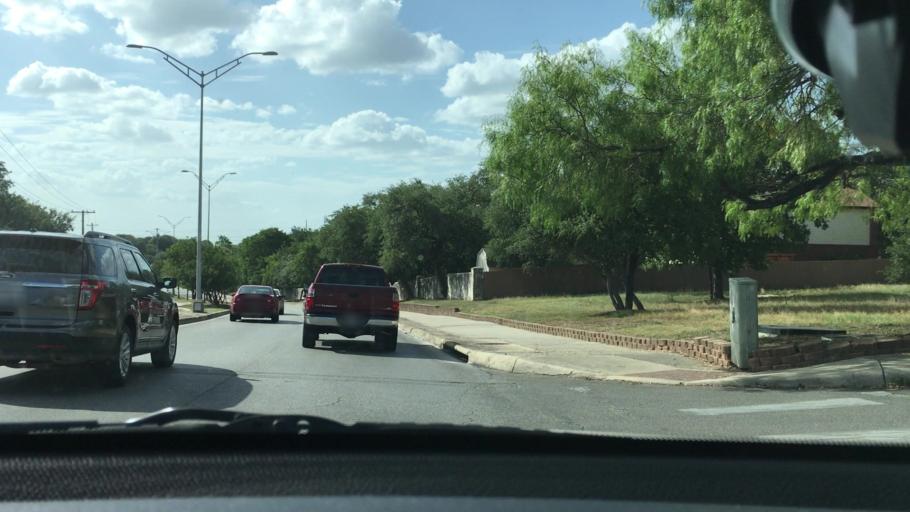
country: US
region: Texas
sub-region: Bexar County
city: Selma
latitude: 29.5820
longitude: -98.2824
